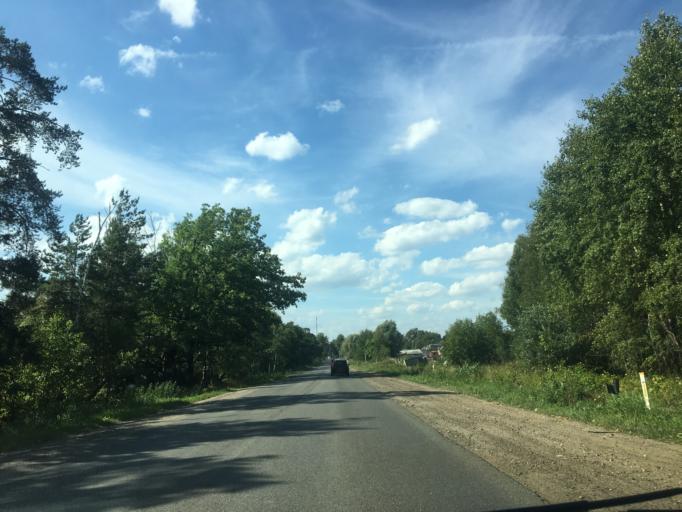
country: RU
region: Moskovskaya
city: Vidnoye
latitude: 55.5275
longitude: 37.6740
